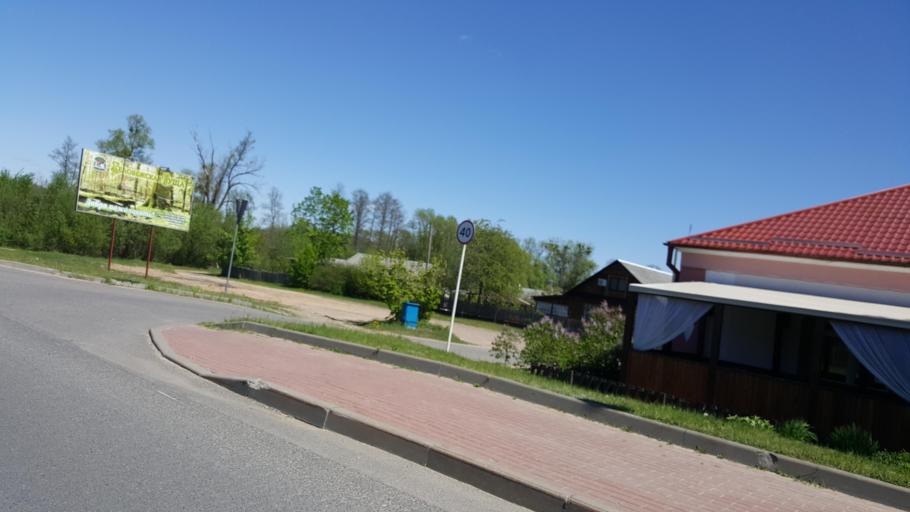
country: BY
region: Brest
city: Kamyanyuki
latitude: 52.5623
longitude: 23.8001
